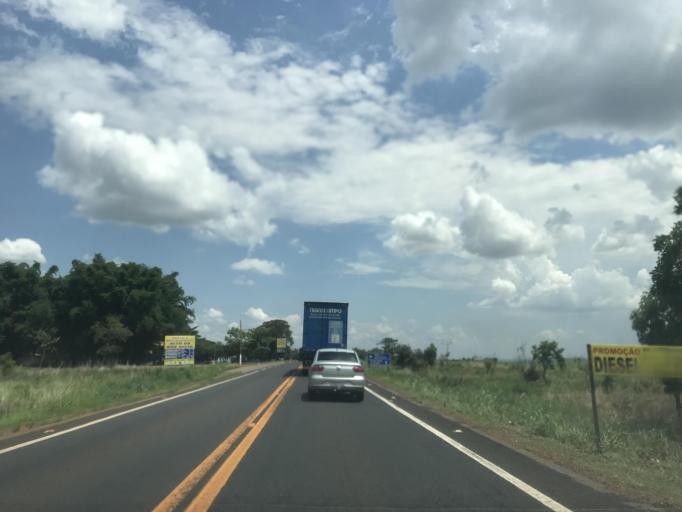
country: BR
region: Goias
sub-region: Caldas Novas
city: Caldas Novas
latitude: -17.4686
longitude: -48.7597
